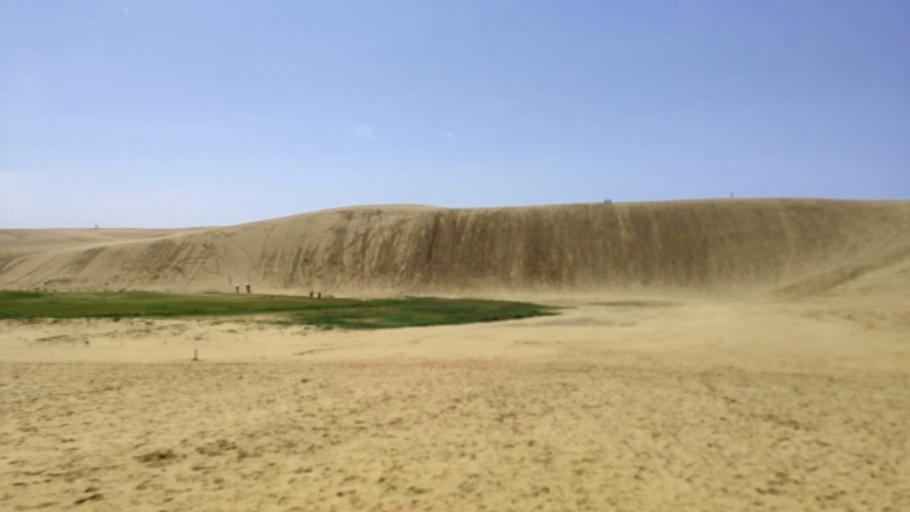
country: JP
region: Tottori
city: Tottori
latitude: 35.5437
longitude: 134.2341
